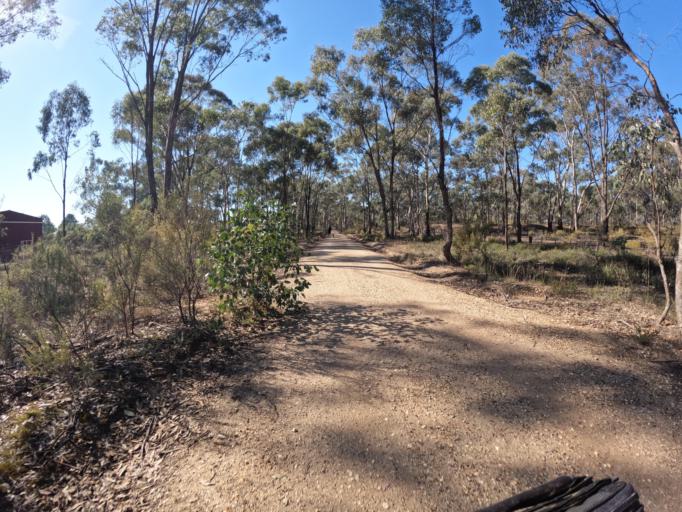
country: AU
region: Victoria
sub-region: Greater Bendigo
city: Kennington
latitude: -36.7805
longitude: 144.3837
